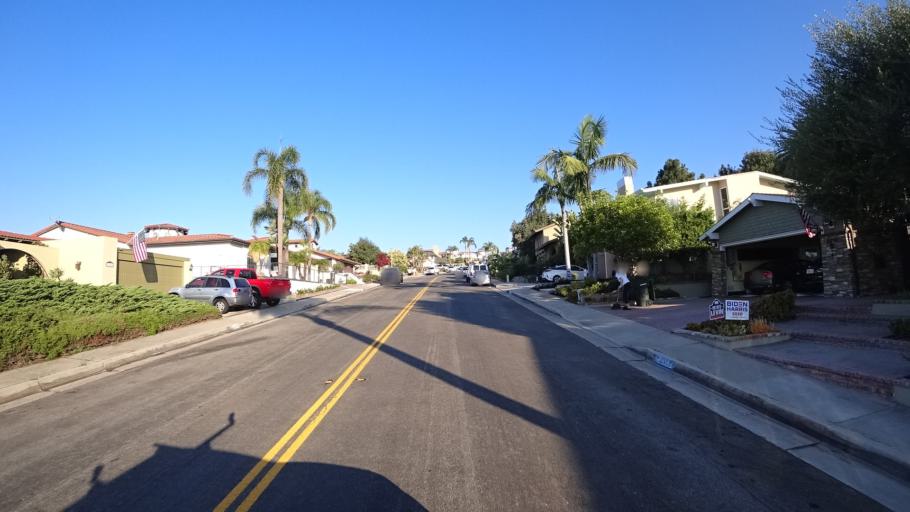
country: US
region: California
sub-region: Orange County
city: San Clemente
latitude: 33.4162
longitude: -117.5966
